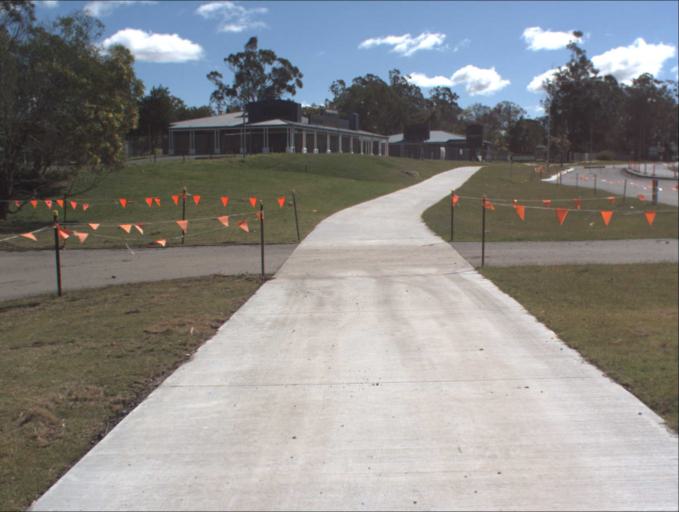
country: AU
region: Queensland
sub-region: Logan
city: Waterford West
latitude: -27.6935
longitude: 153.1022
